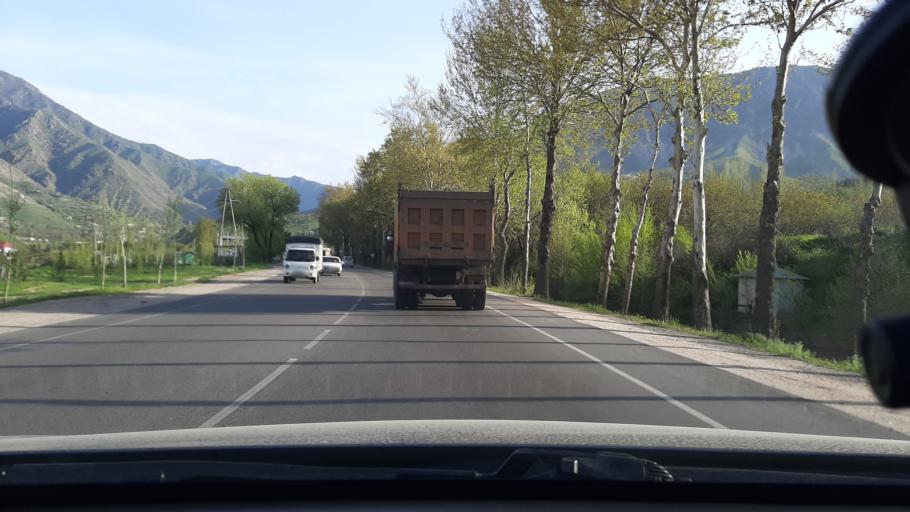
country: TJ
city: Varzob
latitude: 38.6801
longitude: 68.7913
